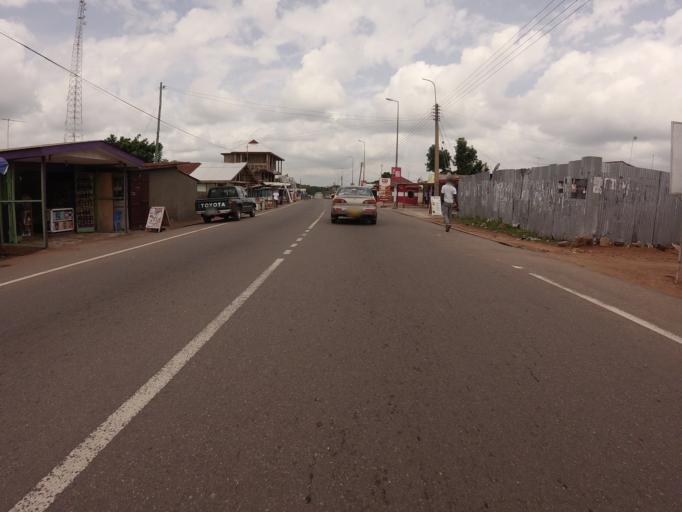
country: GH
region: Volta
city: Ho
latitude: 6.6025
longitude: 0.4707
